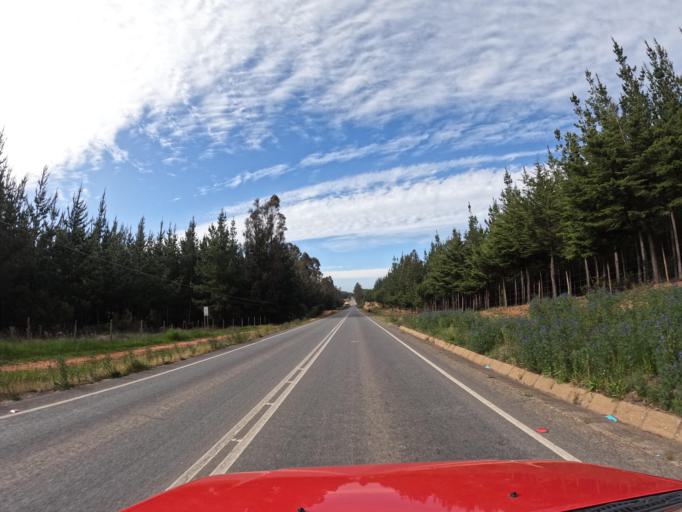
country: CL
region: O'Higgins
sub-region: Provincia de Colchagua
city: Santa Cruz
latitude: -34.3323
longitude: -71.8745
